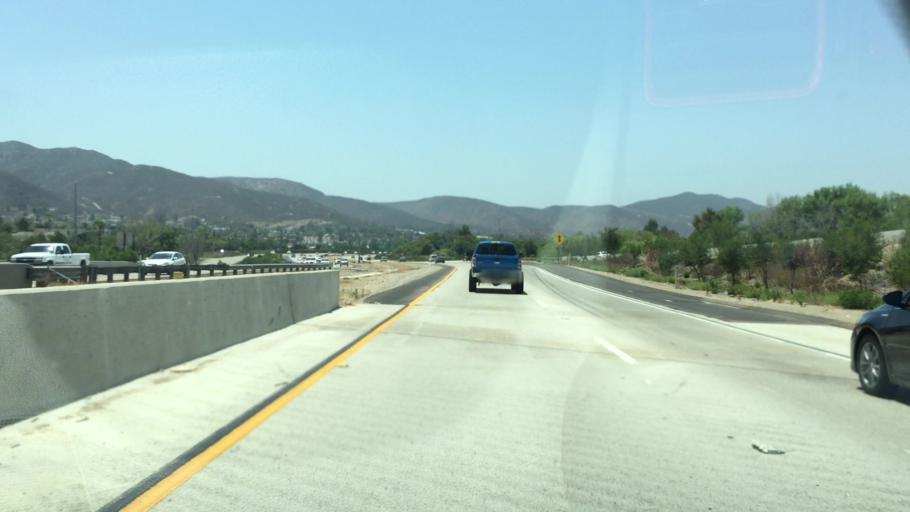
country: US
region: California
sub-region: San Diego County
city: Santee
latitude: 32.8368
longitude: -117.0058
